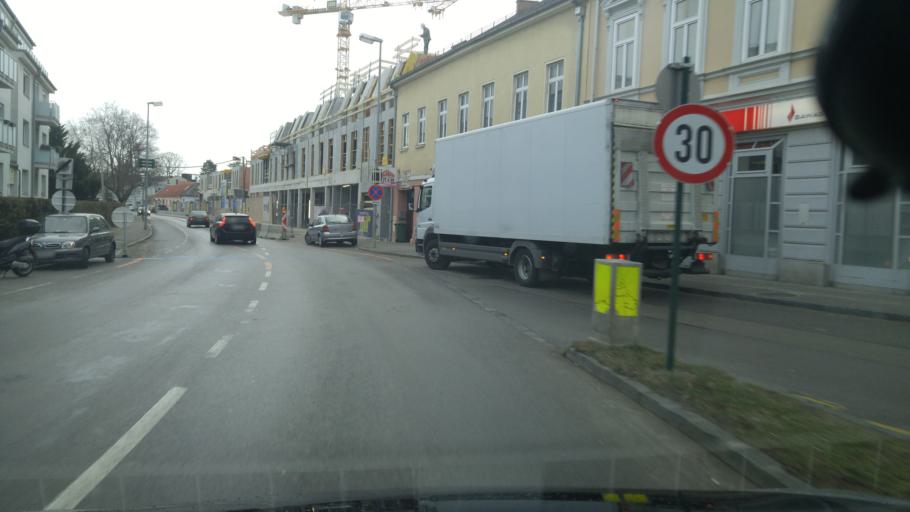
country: AT
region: Lower Austria
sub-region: Politischer Bezirk Baden
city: Bad Voslau
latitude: 47.9647
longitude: 16.2141
